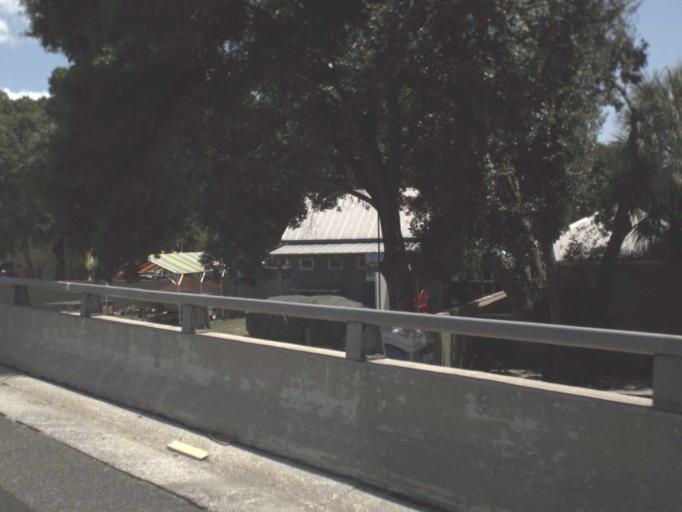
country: US
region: Florida
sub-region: Hillsborough County
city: Tampa
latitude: 27.9392
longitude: -82.4768
